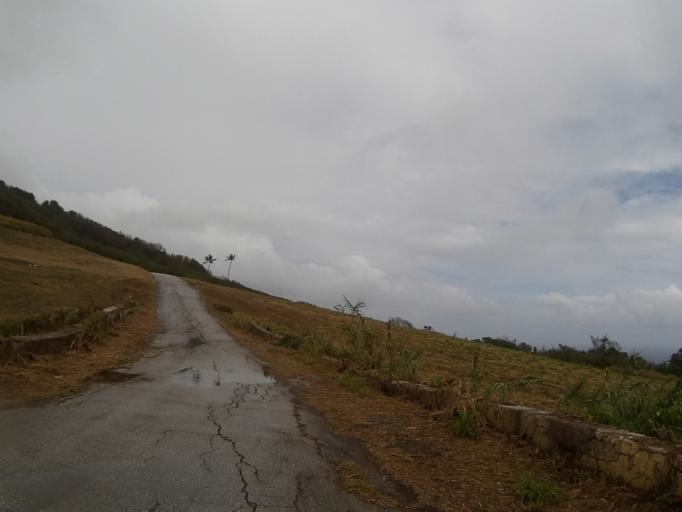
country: BB
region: Saint Andrew
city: Greenland
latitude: 13.2739
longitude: -59.5817
